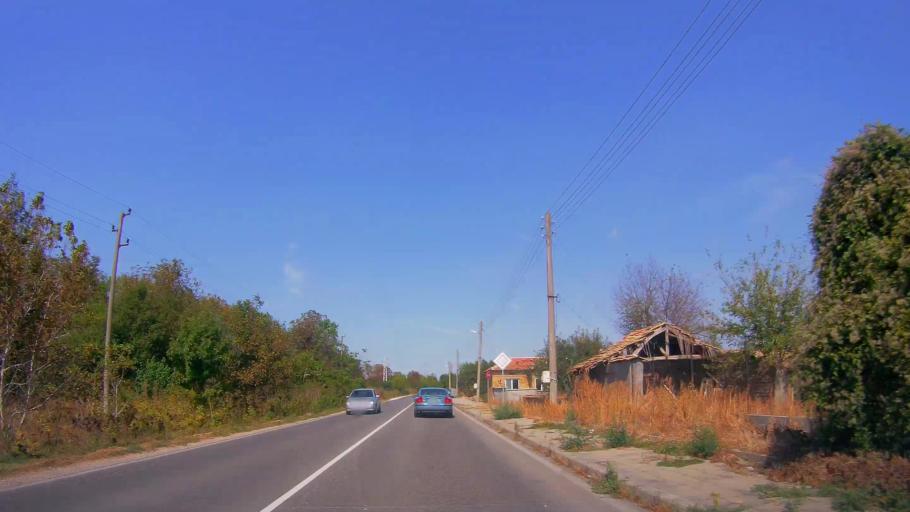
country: BG
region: Shumen
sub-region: Obshtina Smyadovo
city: Smyadovo
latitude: 43.1799
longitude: 27.0069
